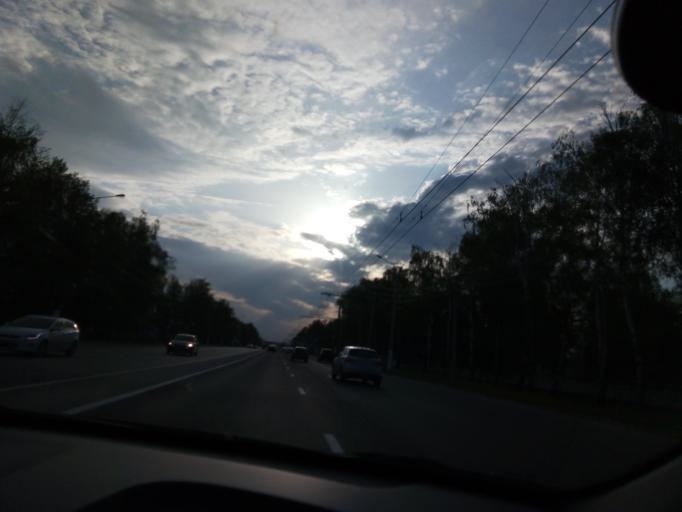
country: RU
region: Chuvashia
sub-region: Cheboksarskiy Rayon
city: Cheboksary
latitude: 56.1264
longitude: 47.3490
